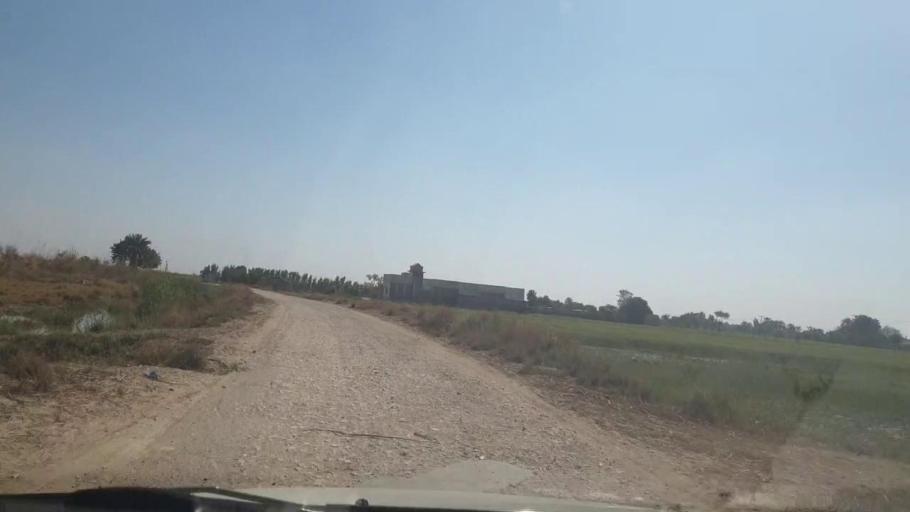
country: PK
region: Sindh
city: Mirpur Khas
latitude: 25.4951
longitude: 69.1366
